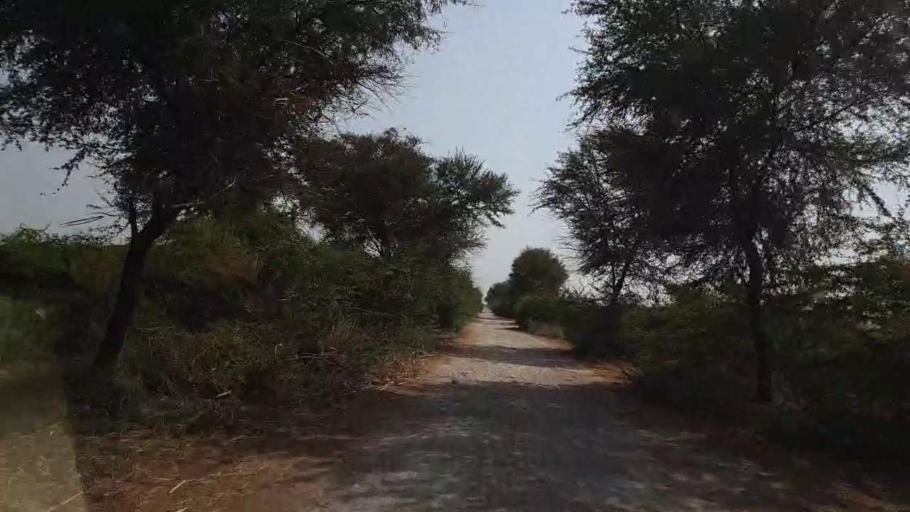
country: PK
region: Sindh
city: Rajo Khanani
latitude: 25.0323
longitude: 68.8730
